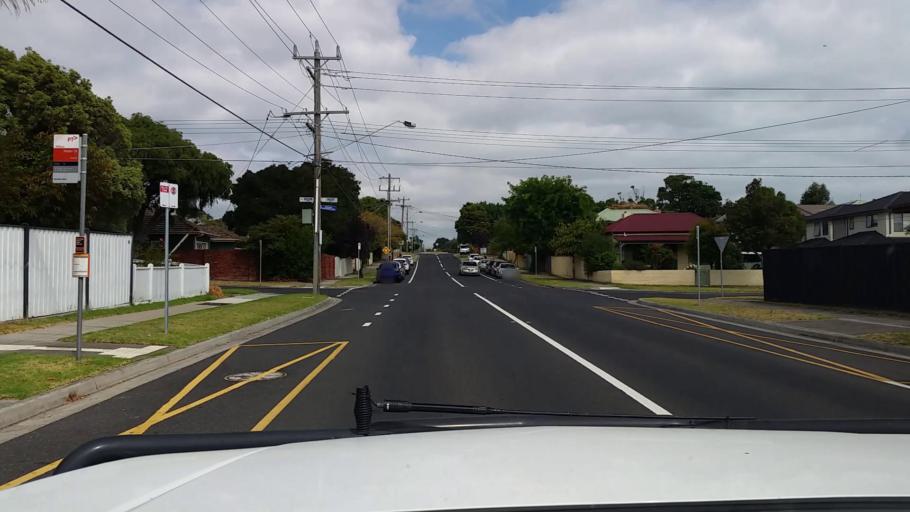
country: AU
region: Victoria
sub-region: Frankston
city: Frankston
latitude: -38.1494
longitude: 145.1203
